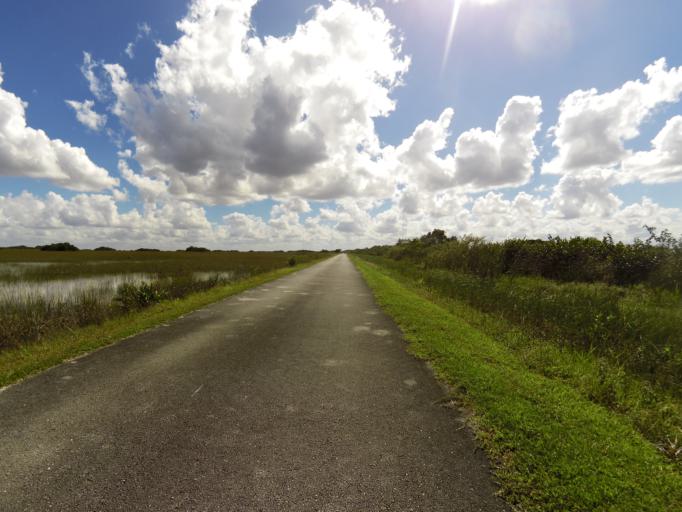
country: US
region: Florida
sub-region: Miami-Dade County
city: The Hammocks
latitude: 25.6965
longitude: -80.7669
